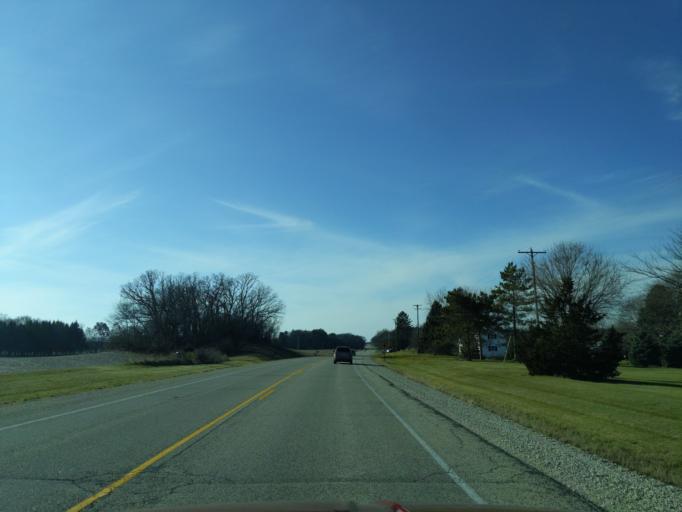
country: US
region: Wisconsin
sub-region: Rock County
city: Milton
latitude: 42.8269
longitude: -88.8823
